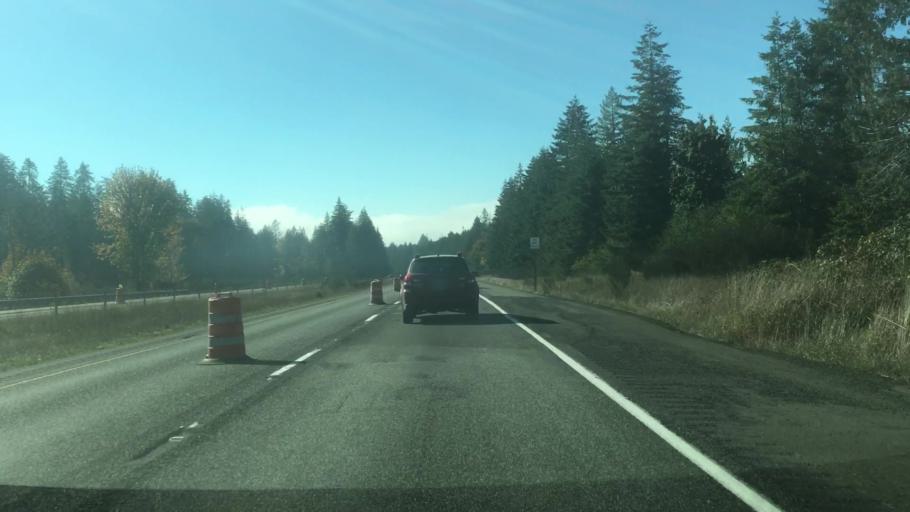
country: US
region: Washington
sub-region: Grays Harbor County
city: McCleary
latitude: 47.0502
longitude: -123.3022
